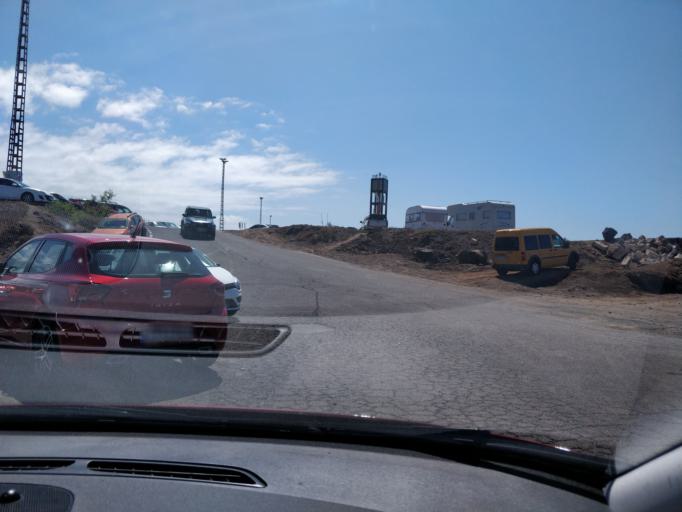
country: ES
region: Canary Islands
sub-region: Provincia de Santa Cruz de Tenerife
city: Puerto de la Cruz
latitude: 28.4185
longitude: -16.5522
